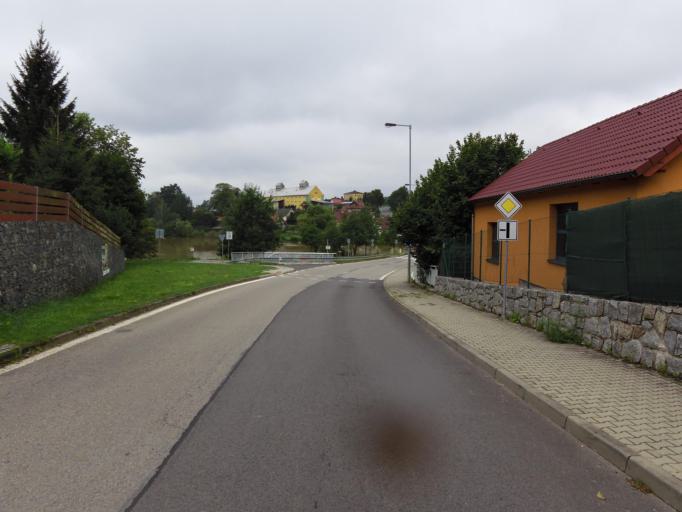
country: CZ
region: Jihocesky
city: Mlada Vozice
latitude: 49.5346
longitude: 14.8084
